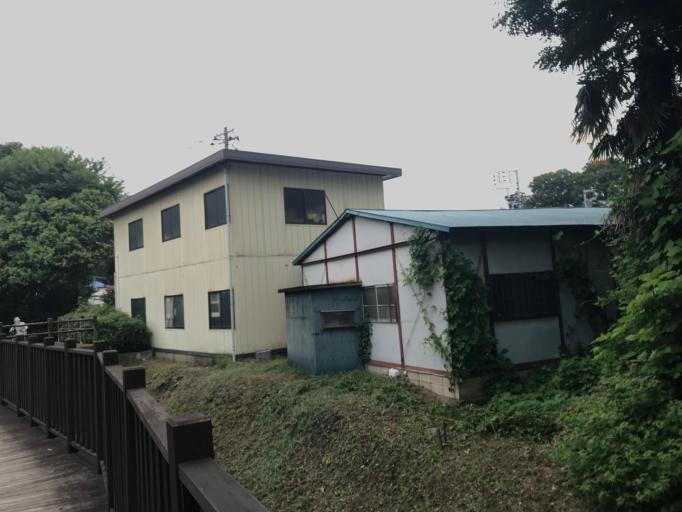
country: JP
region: Tokyo
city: Higashimurayama-shi
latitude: 35.7504
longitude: 139.4924
